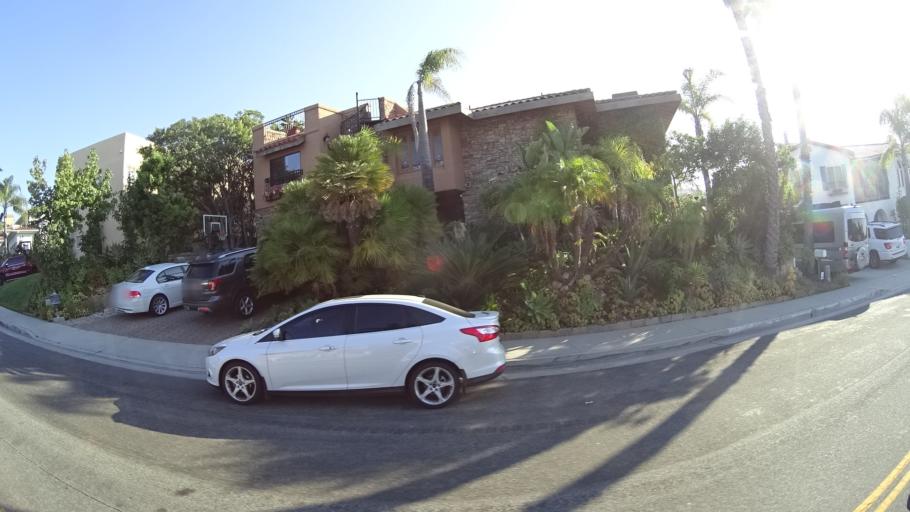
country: US
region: California
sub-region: Orange County
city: San Clemente
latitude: 33.4194
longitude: -117.5980
